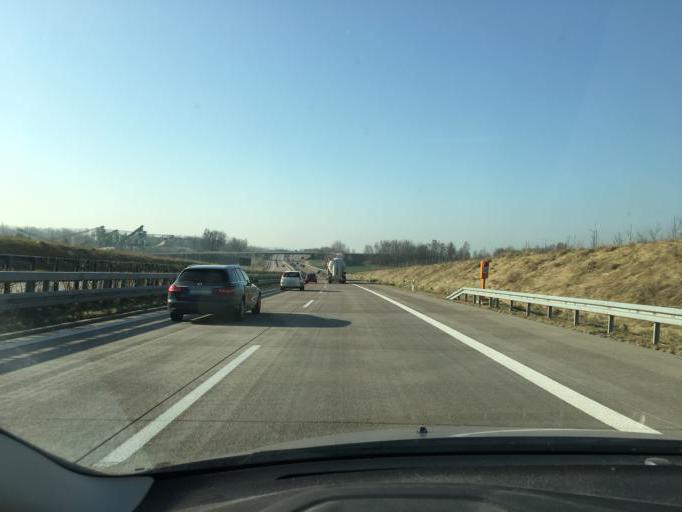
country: DE
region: Saxony
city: Penig
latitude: 50.9624
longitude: 12.6896
